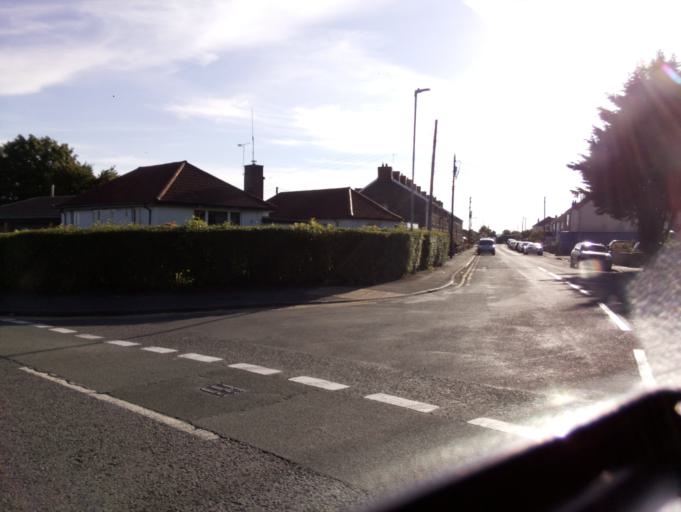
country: GB
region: England
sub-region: South Gloucestershire
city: Kingswood
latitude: 51.4705
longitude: -2.5100
